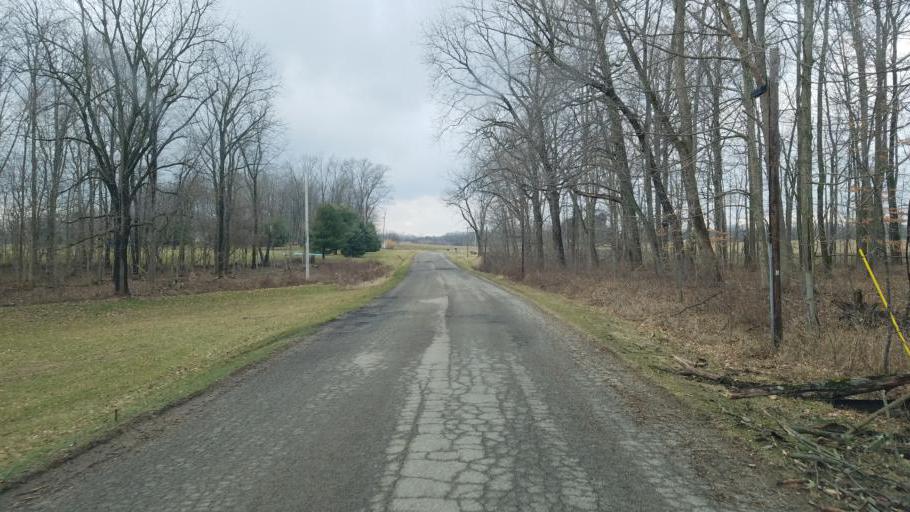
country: US
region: Ohio
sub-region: Morrow County
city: Mount Gilead
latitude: 40.4940
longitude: -82.6960
